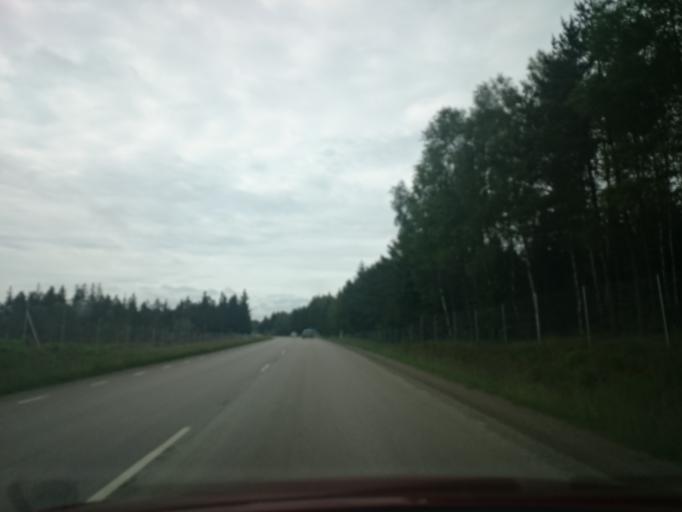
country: SE
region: Vaestra Goetaland
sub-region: Harryda Kommun
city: Hindas
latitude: 57.6804
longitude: 12.3585
